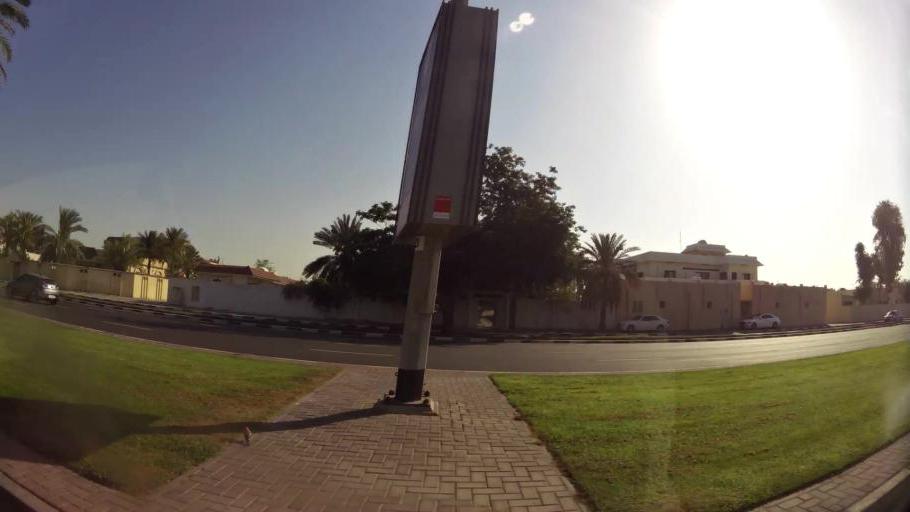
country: AE
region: Ash Shariqah
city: Sharjah
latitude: 25.2655
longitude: 55.3681
